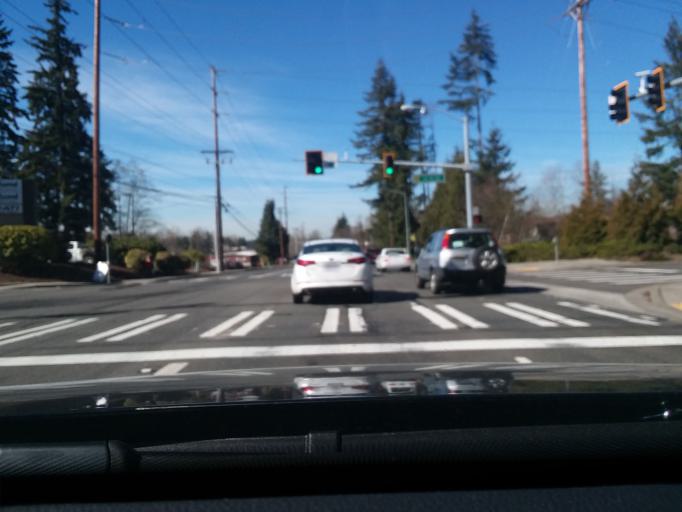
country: US
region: Washington
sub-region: Pierce County
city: South Hill
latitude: 47.1547
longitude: -122.2815
